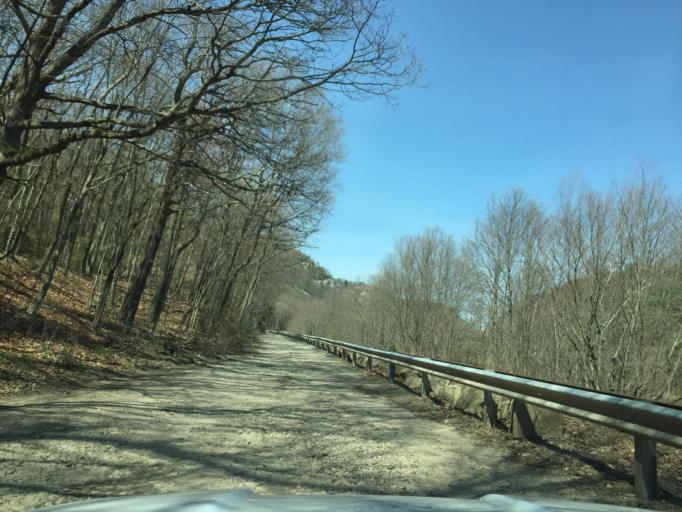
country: US
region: Connecticut
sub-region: New Haven County
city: Naugatuck
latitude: 41.4470
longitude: -73.0691
